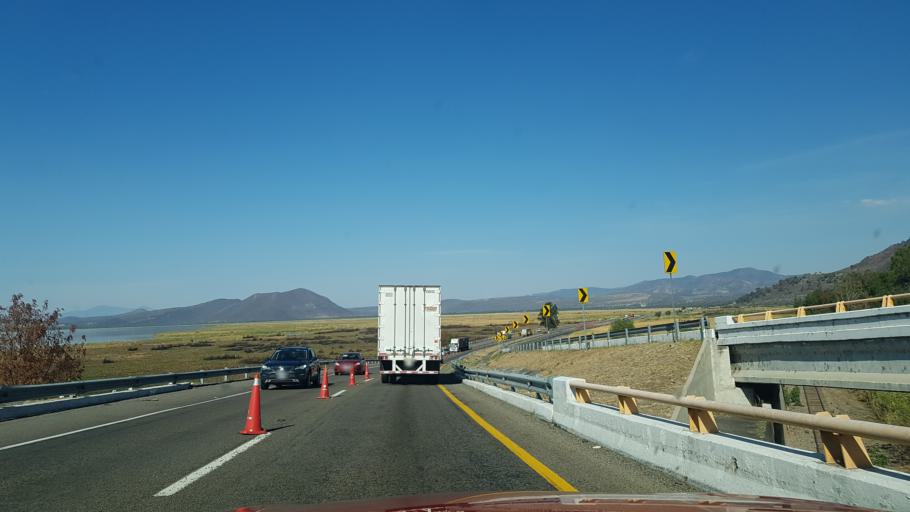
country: MX
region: Michoacan
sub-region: Zinapecuaro
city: Jose Maria Morelos (La Yegueeria)
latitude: 19.8959
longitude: -100.8971
